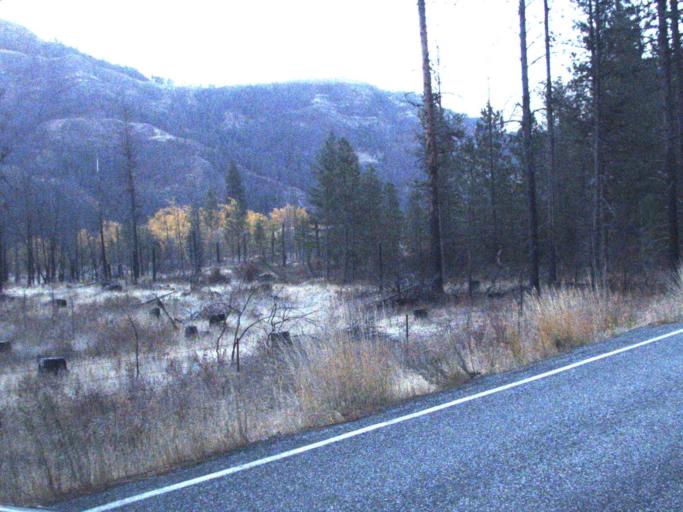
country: US
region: Washington
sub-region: Okanogan County
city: Coulee Dam
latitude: 48.2479
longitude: -118.6930
